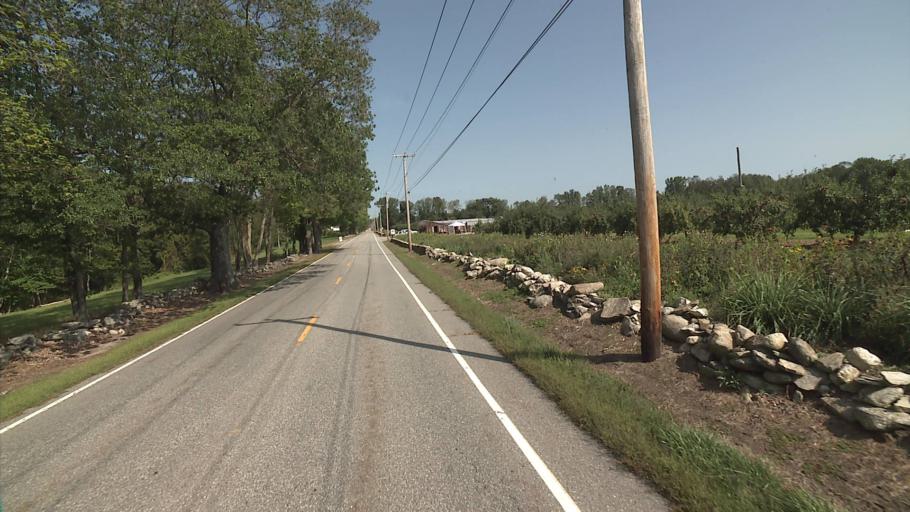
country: US
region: Connecticut
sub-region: Windham County
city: East Brooklyn
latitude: 41.8296
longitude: -71.9587
